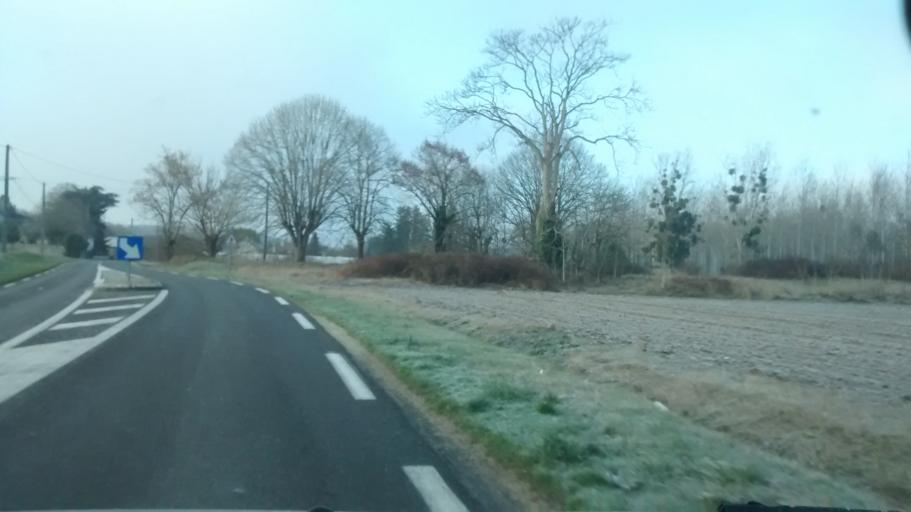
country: FR
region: Centre
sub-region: Departement d'Indre-et-Loire
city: Ballan-Mire
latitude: 47.3618
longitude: 0.6177
